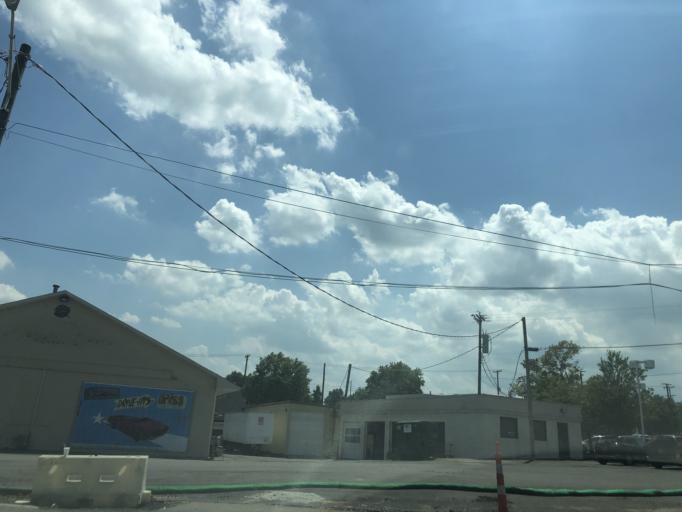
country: US
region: Tennessee
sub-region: Davidson County
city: Lakewood
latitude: 36.1695
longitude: -86.6655
